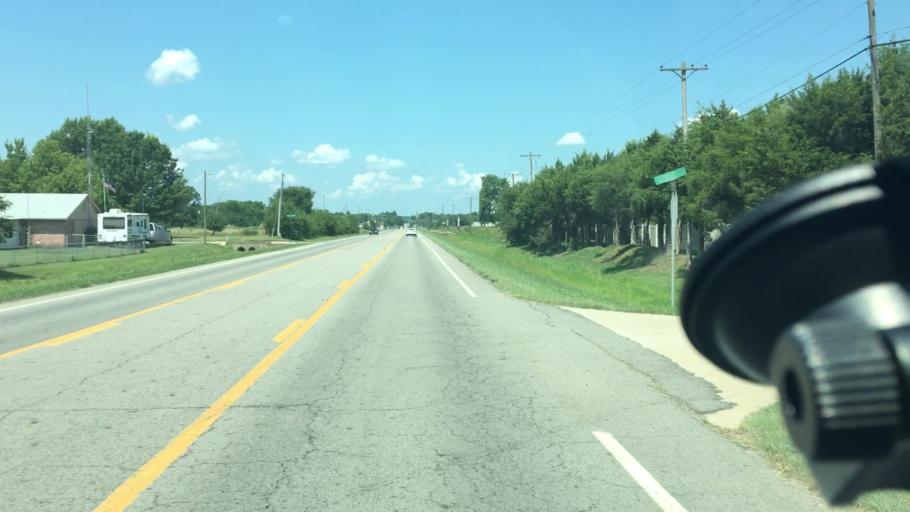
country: US
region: Arkansas
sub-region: Franklin County
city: Charleston
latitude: 35.2968
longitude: -94.0167
